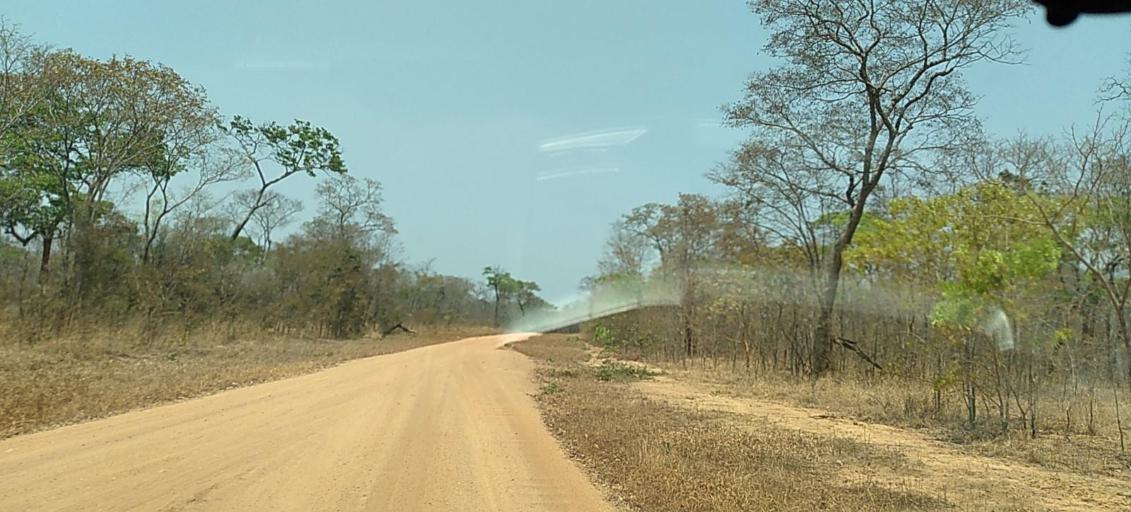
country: ZM
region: Central
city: Mumbwa
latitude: -14.3615
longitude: 26.4799
